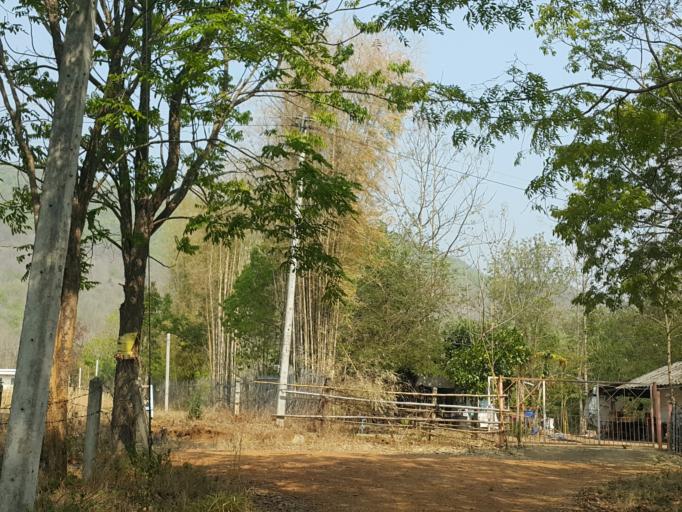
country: TH
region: Chiang Mai
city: Mae On
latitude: 18.7598
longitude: 99.2346
